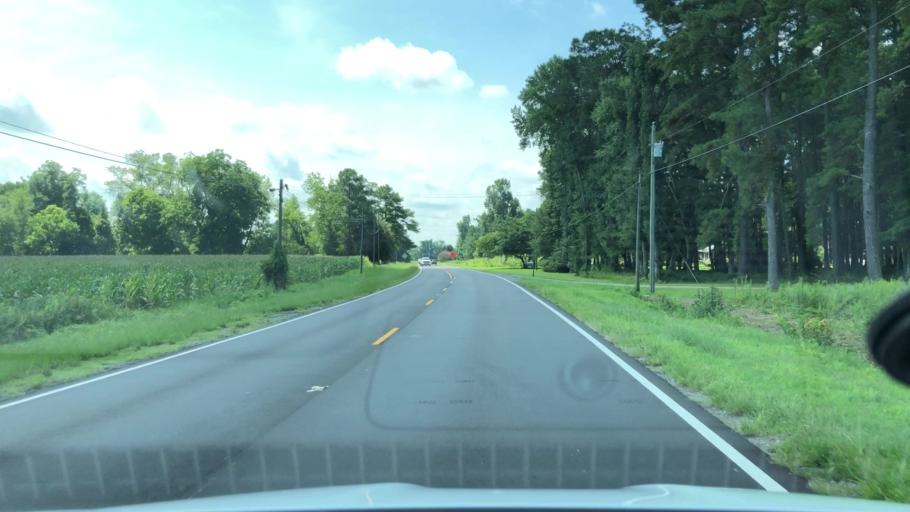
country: US
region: North Carolina
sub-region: Martin County
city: Williamston
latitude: 35.7582
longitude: -77.0753
